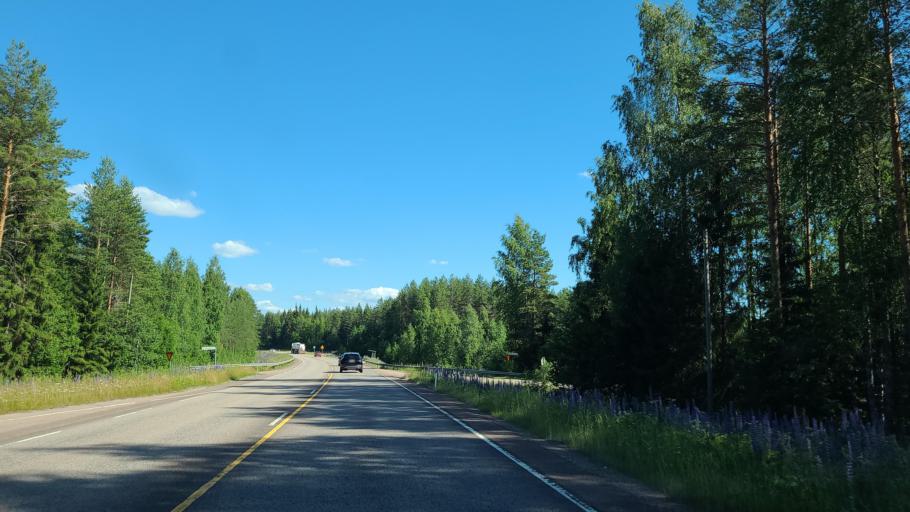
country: FI
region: Central Finland
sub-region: Jyvaeskylae
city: Petaejaevesi
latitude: 62.2687
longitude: 25.4260
